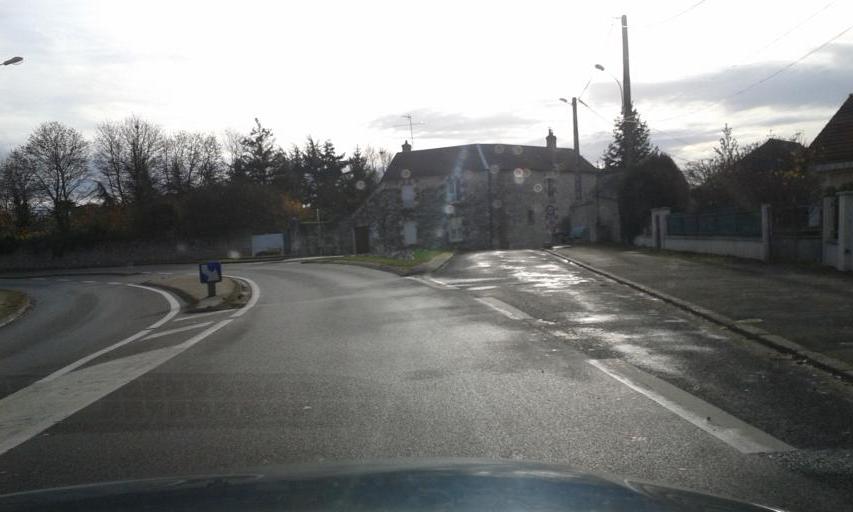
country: FR
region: Centre
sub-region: Departement du Loiret
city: Beaugency
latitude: 47.7845
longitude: 1.6284
